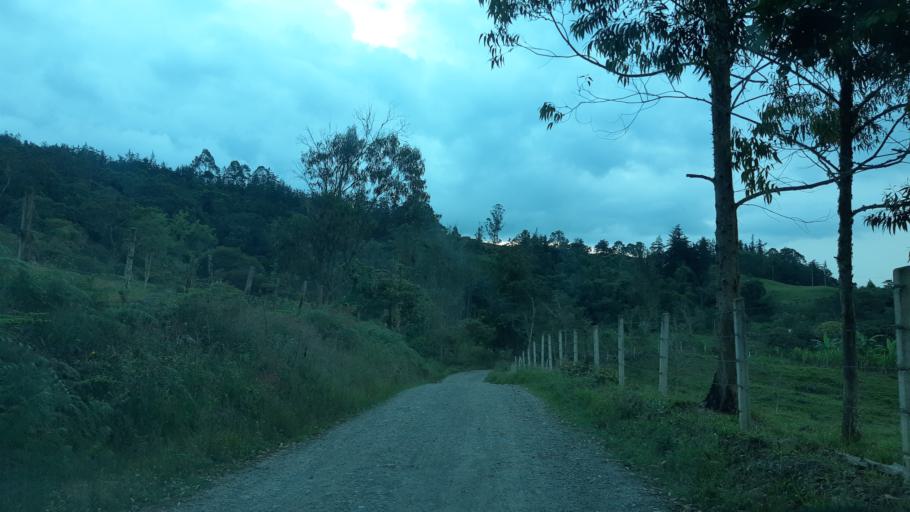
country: CO
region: Boyaca
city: Garagoa
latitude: 5.1111
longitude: -73.3528
